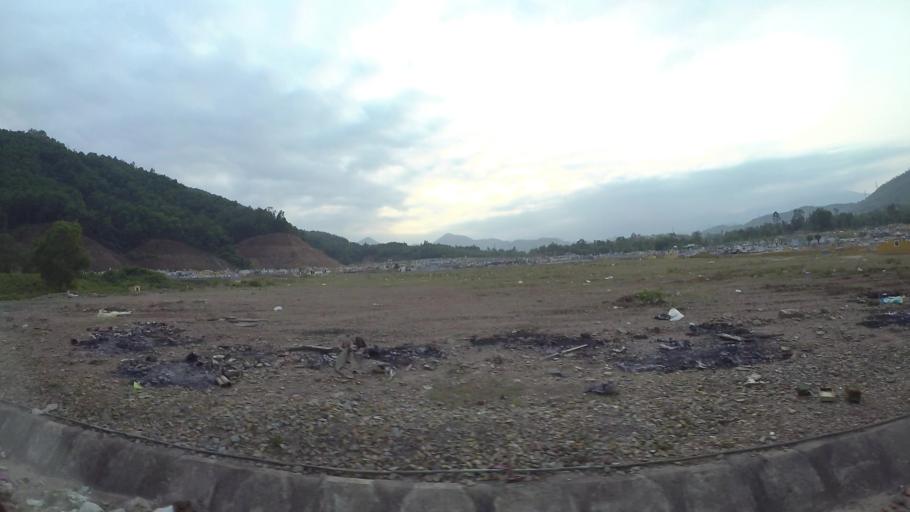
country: VN
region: Da Nang
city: Lien Chieu
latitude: 16.0550
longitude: 108.1234
